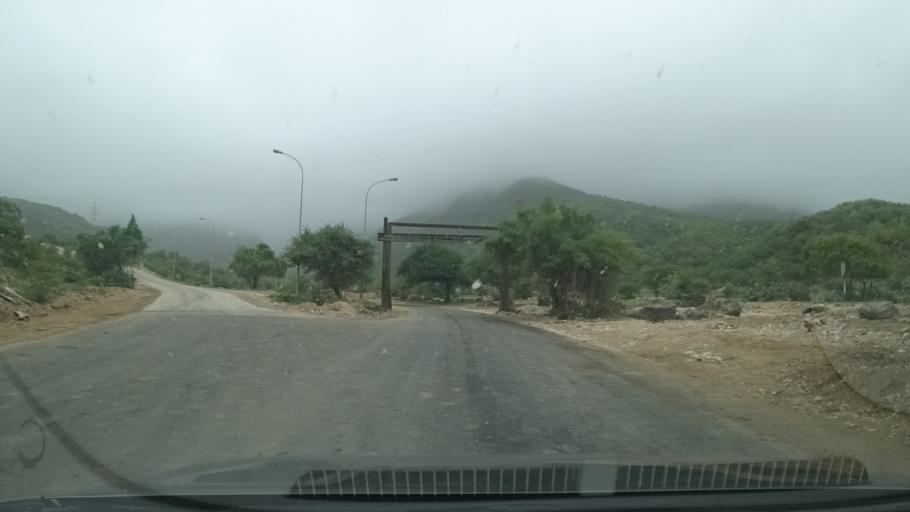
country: OM
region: Zufar
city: Salalah
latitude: 17.1005
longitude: 54.0770
